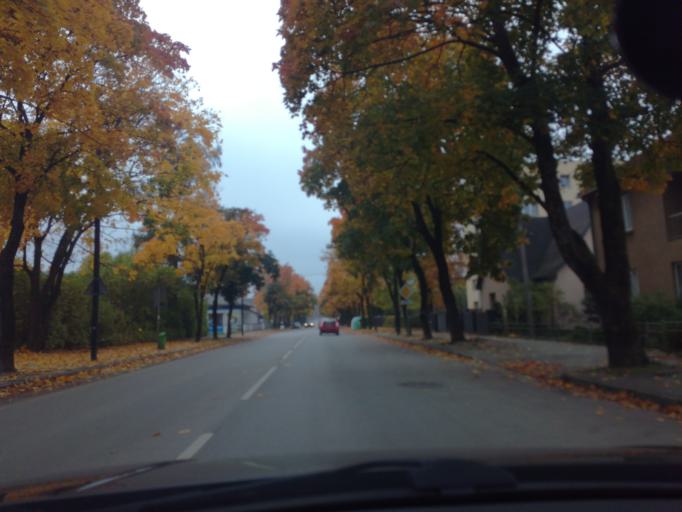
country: LT
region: Alytaus apskritis
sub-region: Alytus
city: Alytus
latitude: 54.3916
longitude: 24.0444
